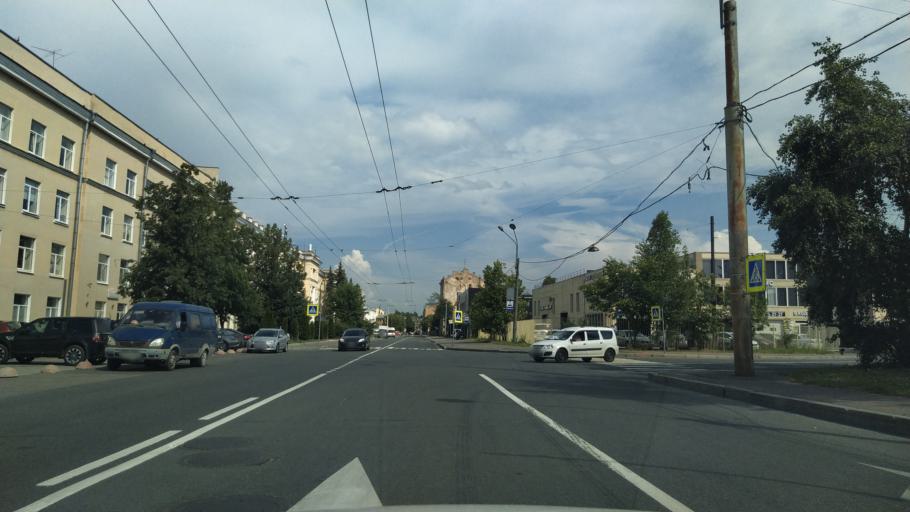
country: RU
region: Leningrad
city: Finlyandskiy
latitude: 59.9655
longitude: 30.3724
